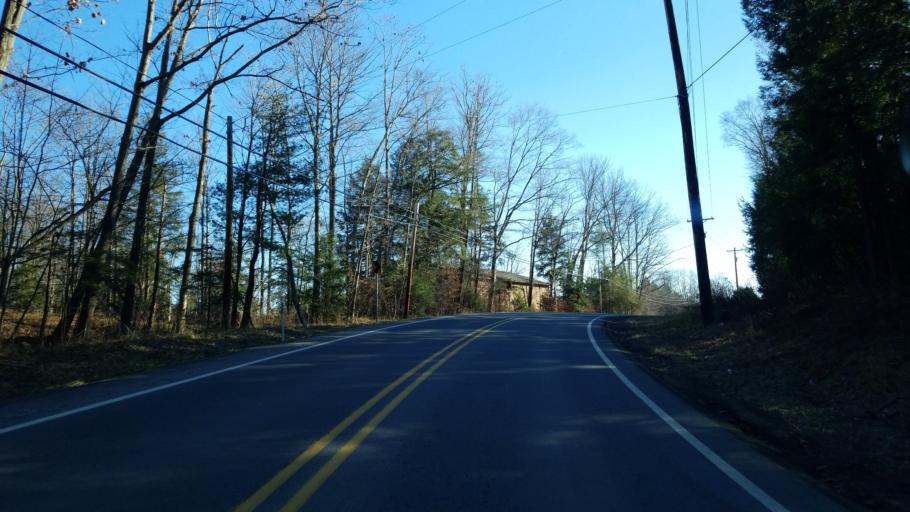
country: US
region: Pennsylvania
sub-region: Jefferson County
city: Falls Creek
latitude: 41.1747
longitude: -78.8360
